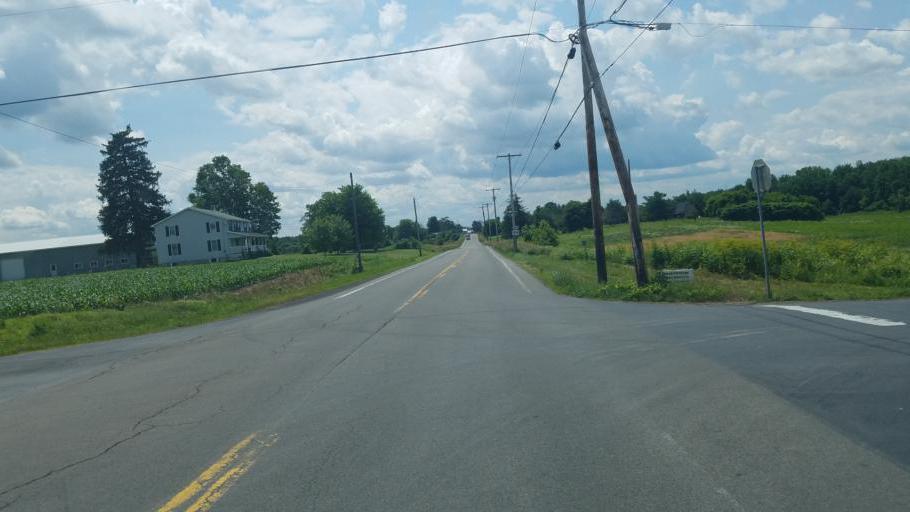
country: US
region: New York
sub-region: Wayne County
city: Clyde
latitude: 43.1129
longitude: -76.8695
